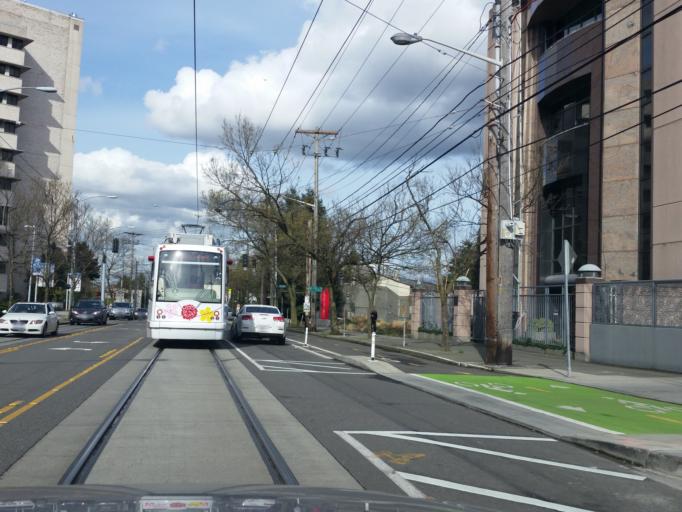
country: US
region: Washington
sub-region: King County
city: Seattle
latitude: 47.6085
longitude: -122.3208
